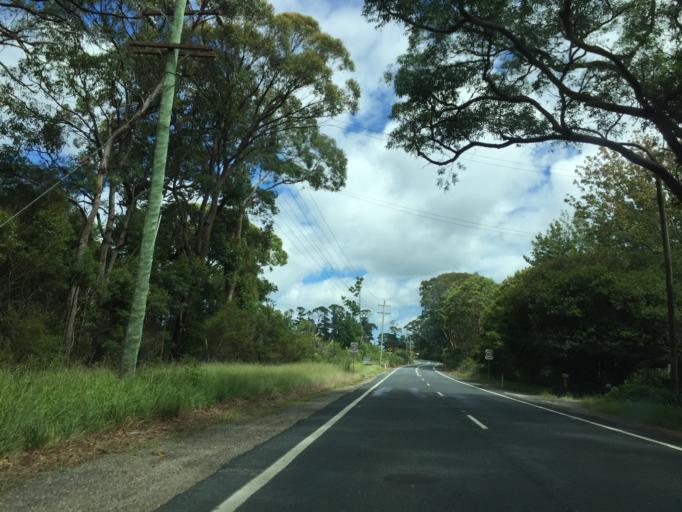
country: AU
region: New South Wales
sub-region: Hawkesbury
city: Richmond
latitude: -33.5160
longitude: 150.5858
